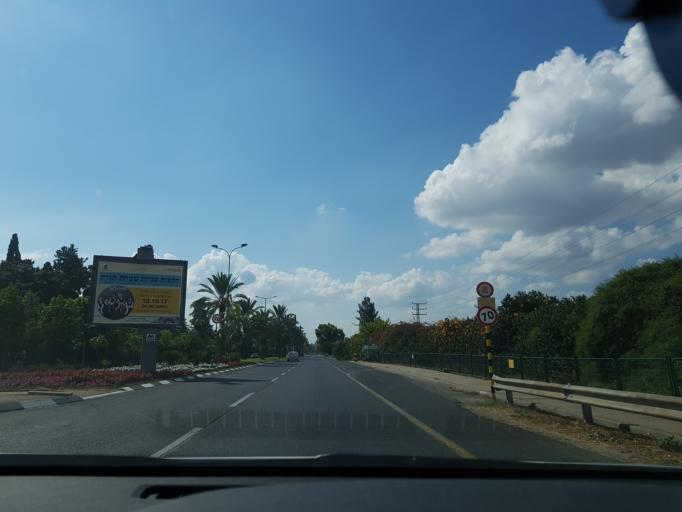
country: IL
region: Central District
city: Ness Ziona
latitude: 31.9413
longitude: 34.8004
